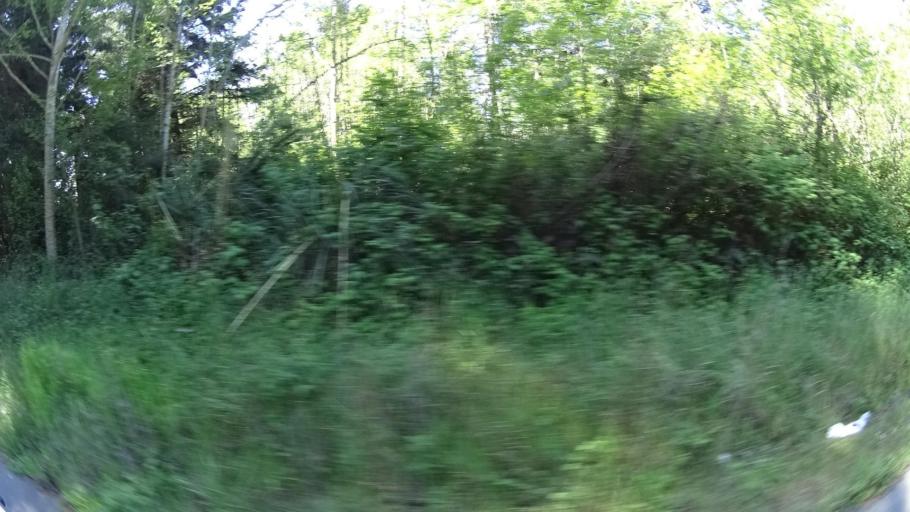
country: US
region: California
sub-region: Humboldt County
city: McKinleyville
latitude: 40.9556
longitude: -124.0862
